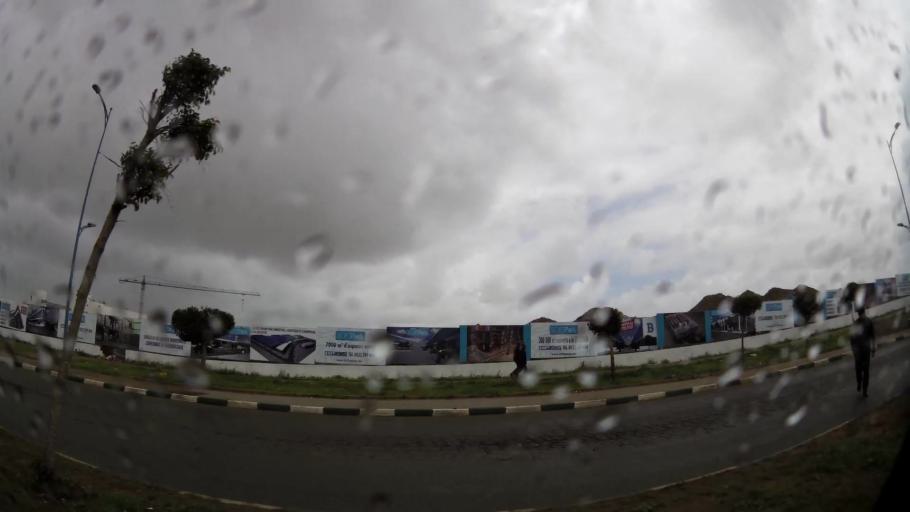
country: MA
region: Grand Casablanca
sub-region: Mediouna
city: Tit Mellil
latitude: 33.6218
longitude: -7.5018
